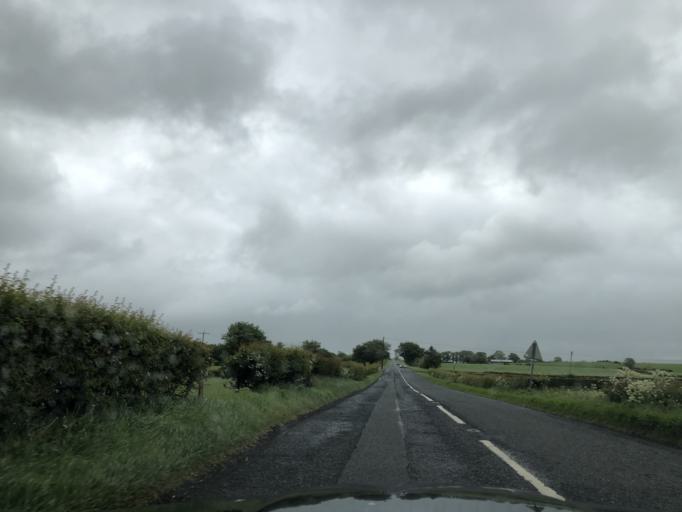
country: GB
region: Northern Ireland
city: Bushmills
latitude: 55.1496
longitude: -6.4396
